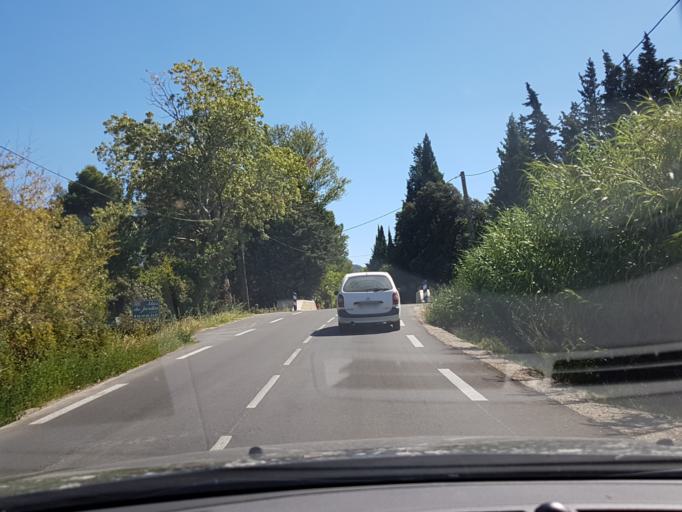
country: FR
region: Provence-Alpes-Cote d'Azur
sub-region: Departement des Bouches-du-Rhone
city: Eygalieres
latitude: 43.7737
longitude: 4.9306
